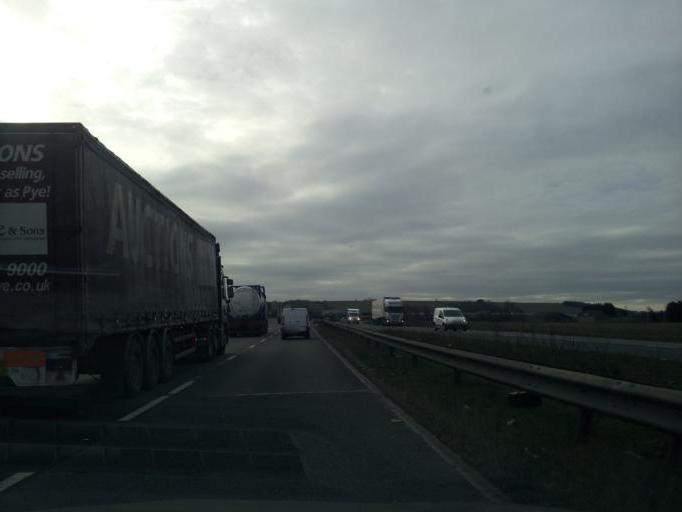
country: GB
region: England
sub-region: Lincolnshire
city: Great Gonerby
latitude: 52.9568
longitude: -0.6857
